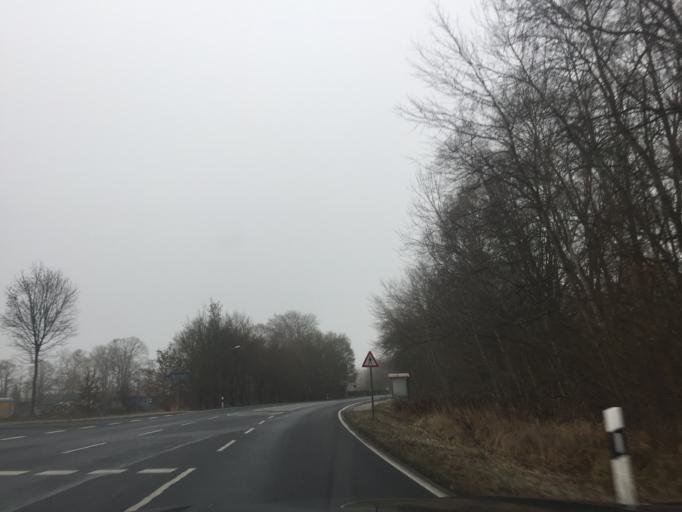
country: DE
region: Brandenburg
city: Hennigsdorf
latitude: 52.6265
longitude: 13.1440
